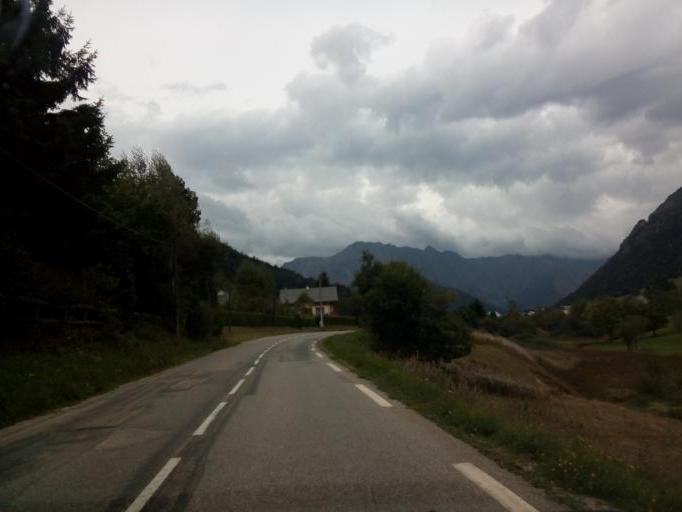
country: FR
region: Rhone-Alpes
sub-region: Departement de l'Isere
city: Vaulnaveys-le-Bas
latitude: 45.0286
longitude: 5.8513
